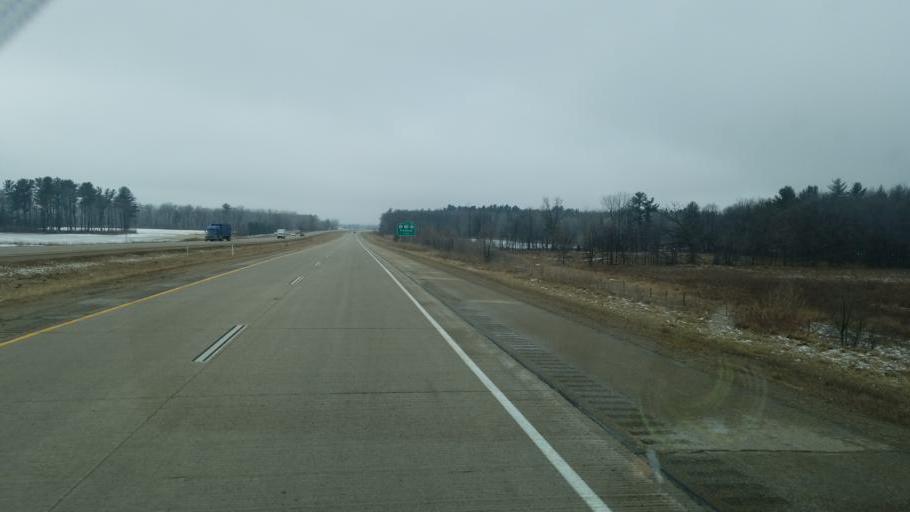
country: US
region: Wisconsin
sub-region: Waupaca County
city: Weyauwega
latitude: 44.2514
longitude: -88.8216
